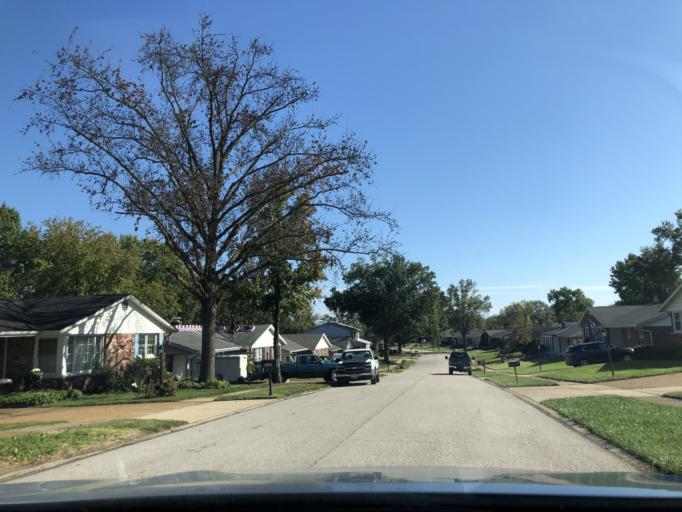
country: US
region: Missouri
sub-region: Saint Louis County
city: Concord
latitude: 38.5039
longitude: -90.3754
